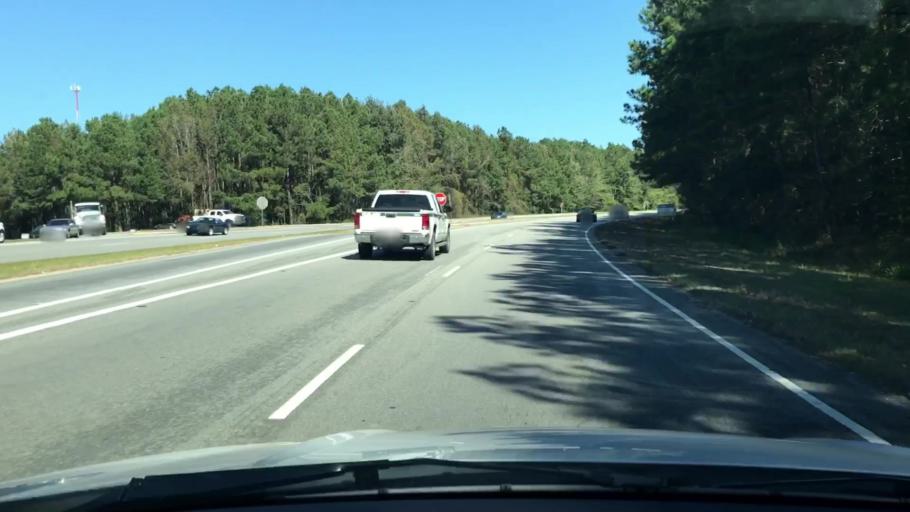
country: US
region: South Carolina
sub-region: Beaufort County
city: Bluffton
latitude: 32.3507
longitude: -80.9237
